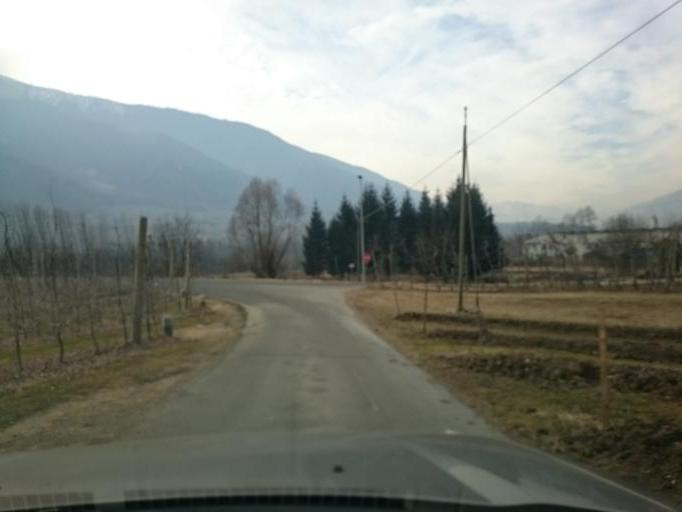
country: IT
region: Lombardy
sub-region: Provincia di Sondrio
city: Lovero
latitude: 46.2375
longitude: 10.2250
